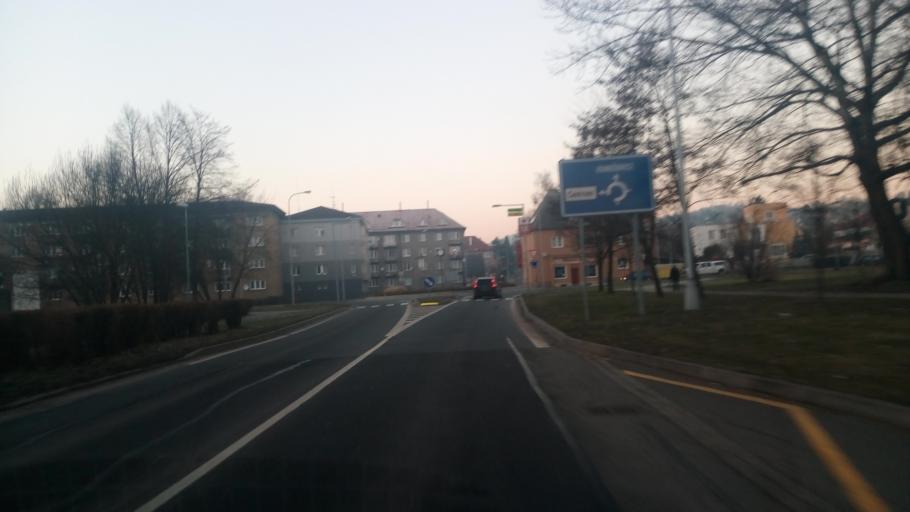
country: CZ
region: Olomoucky
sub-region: Okres Sumperk
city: Sumperk
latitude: 49.9668
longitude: 16.9845
